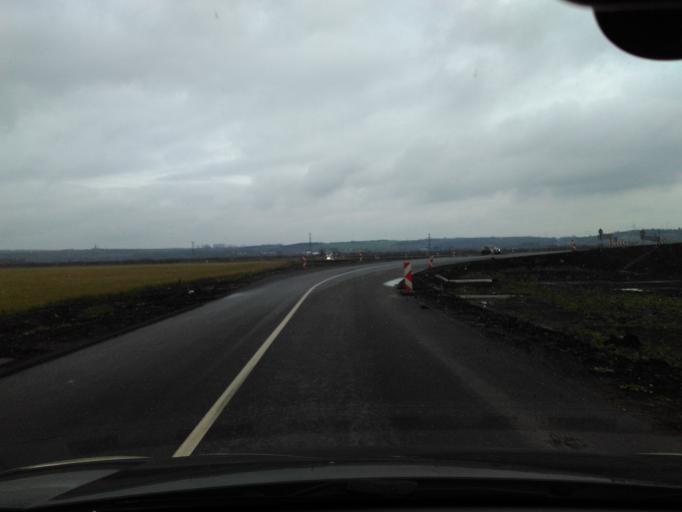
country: HU
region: Heves
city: Hatvan
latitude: 47.6949
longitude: 19.6664
